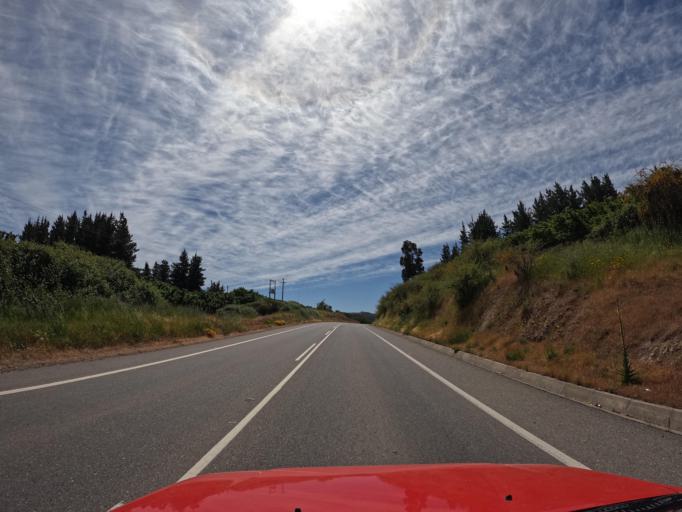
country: CL
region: Maule
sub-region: Provincia de Talca
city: Talca
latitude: -35.2584
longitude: -71.5430
